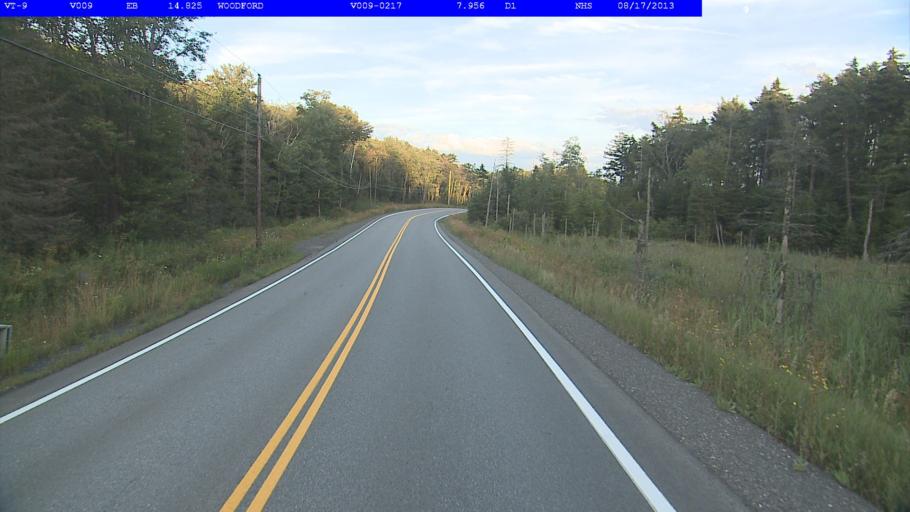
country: US
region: Vermont
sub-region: Bennington County
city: Bennington
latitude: 42.8950
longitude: -73.0396
